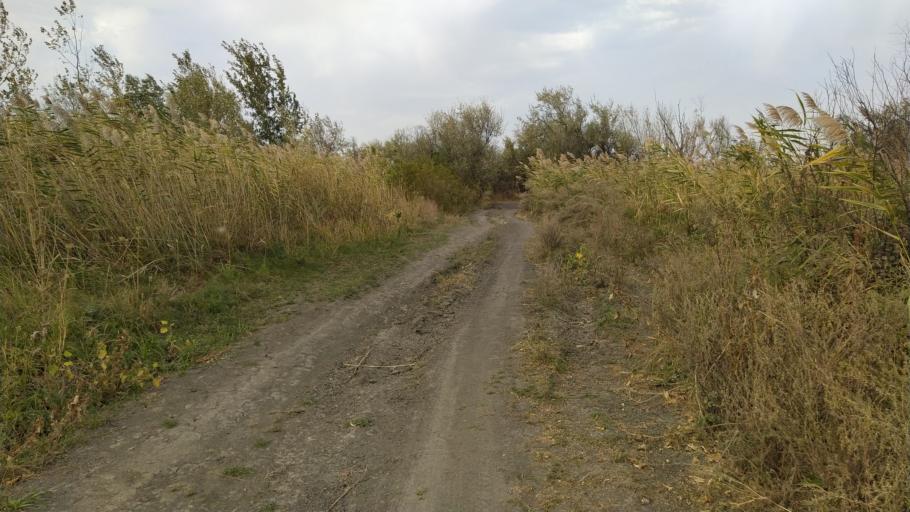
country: RU
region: Rostov
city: Kuleshovka
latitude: 47.1461
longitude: 39.5861
